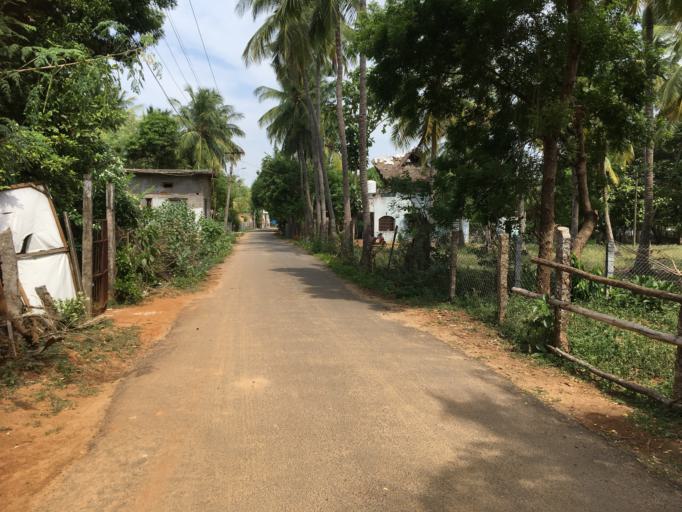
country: IN
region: Tamil Nadu
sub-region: Villupuram
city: Auroville
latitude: 12.0116
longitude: 79.7980
